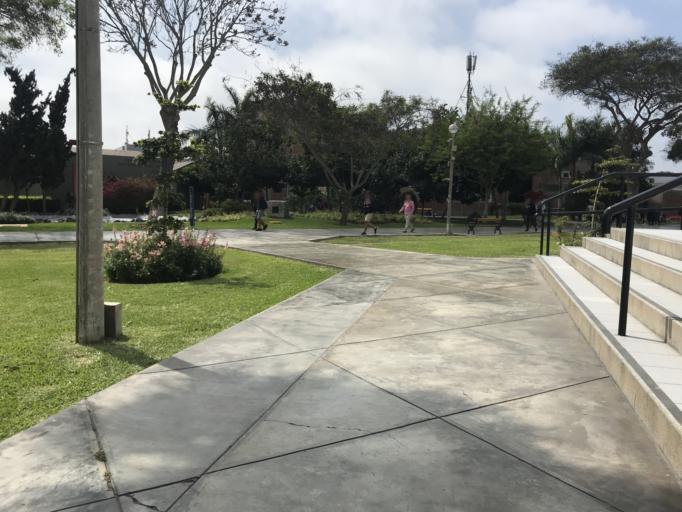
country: PE
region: Callao
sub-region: Callao
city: Callao
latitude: -12.0697
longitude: -77.0795
